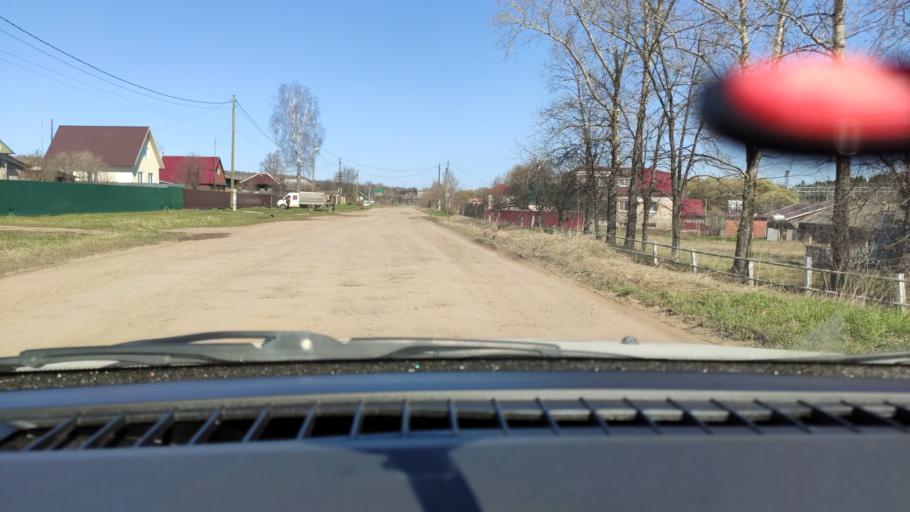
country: RU
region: Perm
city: Bershet'
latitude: 57.7314
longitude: 56.3787
